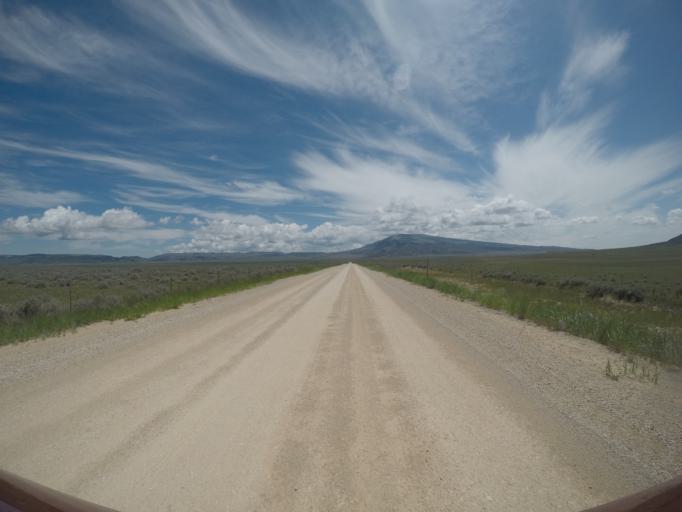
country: US
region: Wyoming
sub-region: Park County
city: Powell
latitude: 45.2051
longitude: -108.7510
